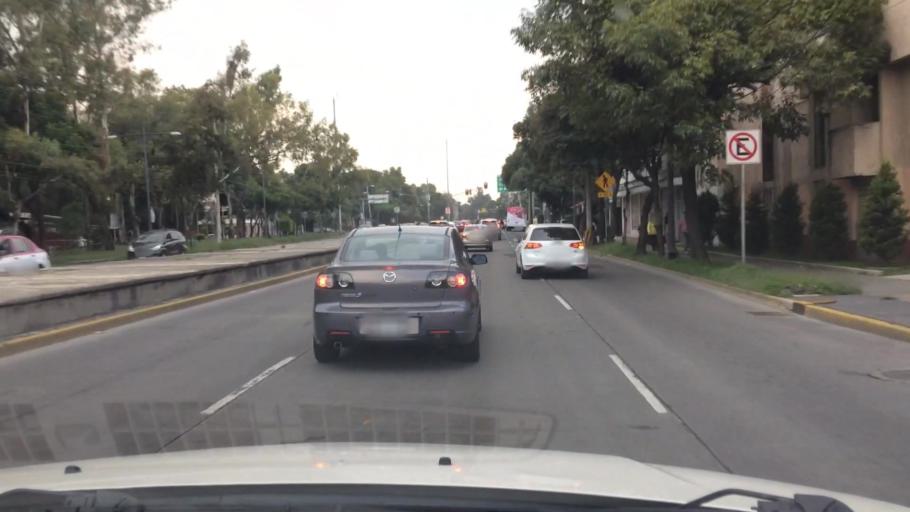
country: MX
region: Mexico City
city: Coyoacan
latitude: 19.3266
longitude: -99.1405
